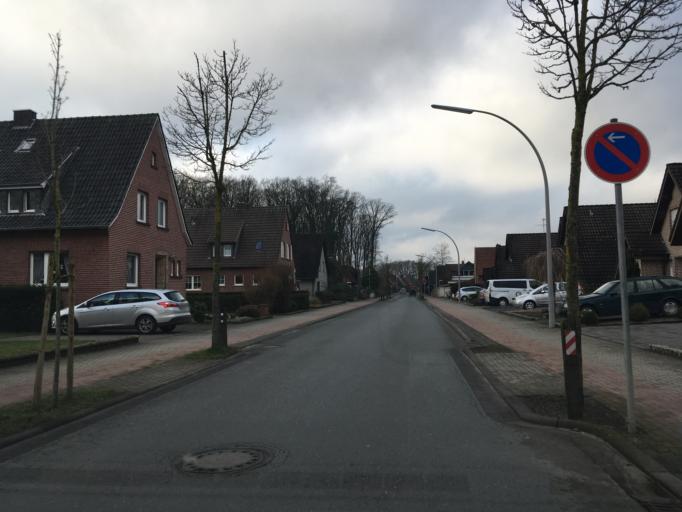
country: DE
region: North Rhine-Westphalia
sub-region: Regierungsbezirk Munster
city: Gescher
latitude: 51.9485
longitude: 7.0058
